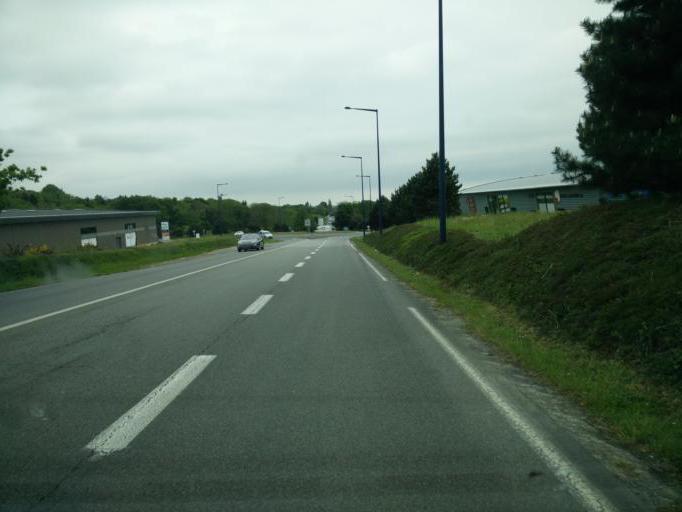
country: FR
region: Brittany
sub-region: Departement du Finistere
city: Concarneau
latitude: 47.8871
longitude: -3.9142
